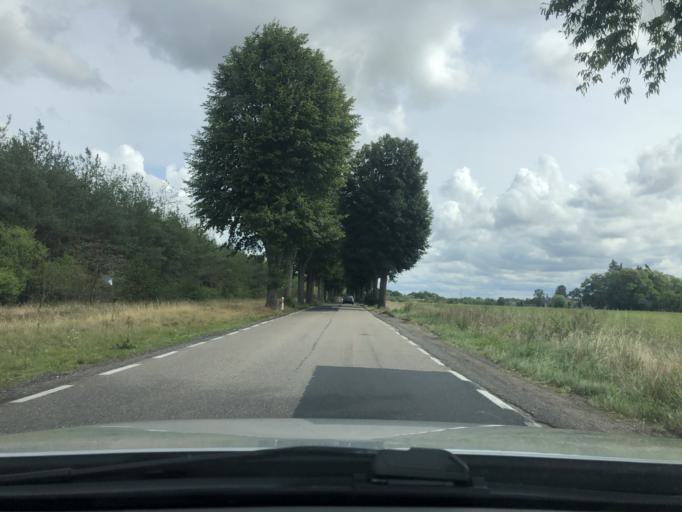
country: PL
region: Greater Poland Voivodeship
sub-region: Powiat czarnkowsko-trzcianecki
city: Wielen
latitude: 52.9036
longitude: 16.1458
